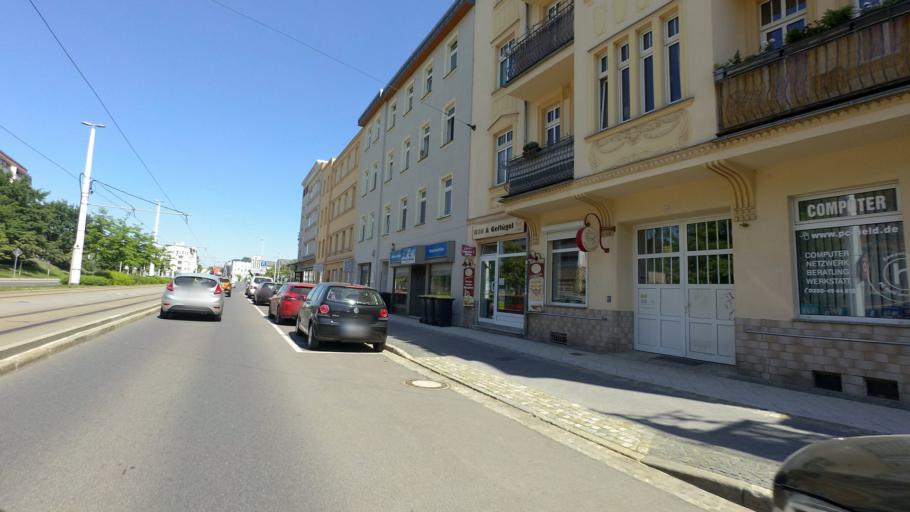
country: DE
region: Brandenburg
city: Cottbus
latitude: 51.7473
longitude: 14.3320
